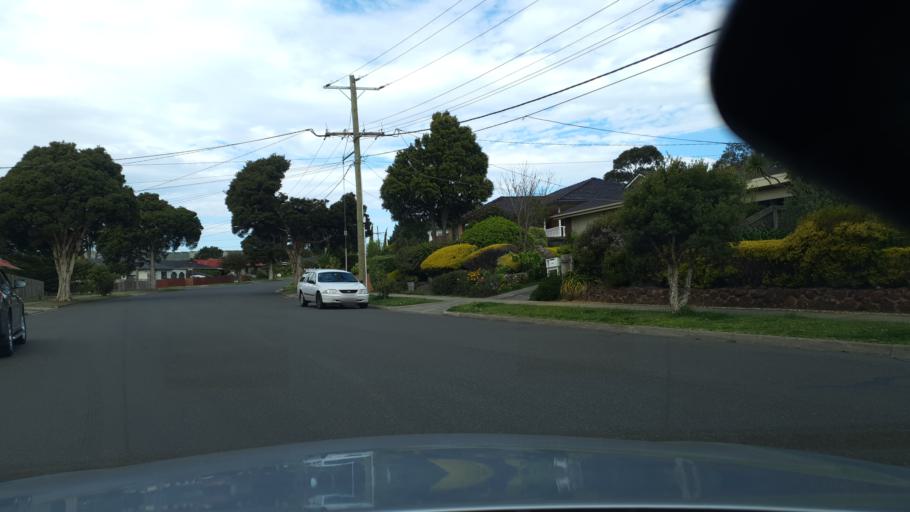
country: AU
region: Victoria
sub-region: Greater Dandenong
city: Noble Park North
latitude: -37.9310
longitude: 145.1839
